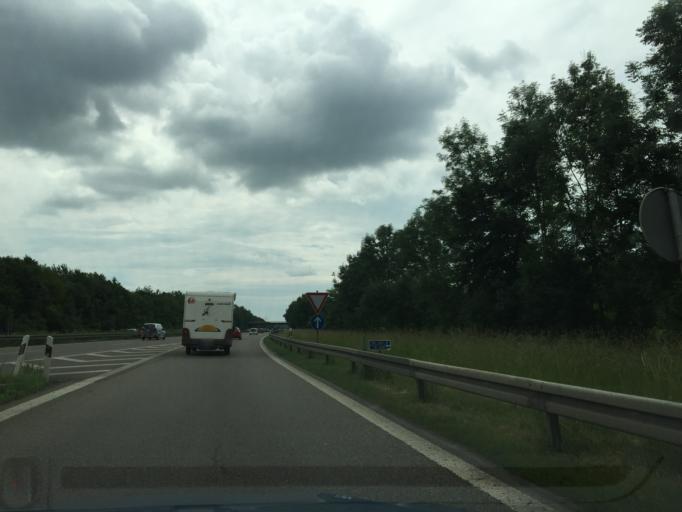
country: DE
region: Bavaria
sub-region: Swabia
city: Neu-Ulm
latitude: 48.3677
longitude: 9.9985
